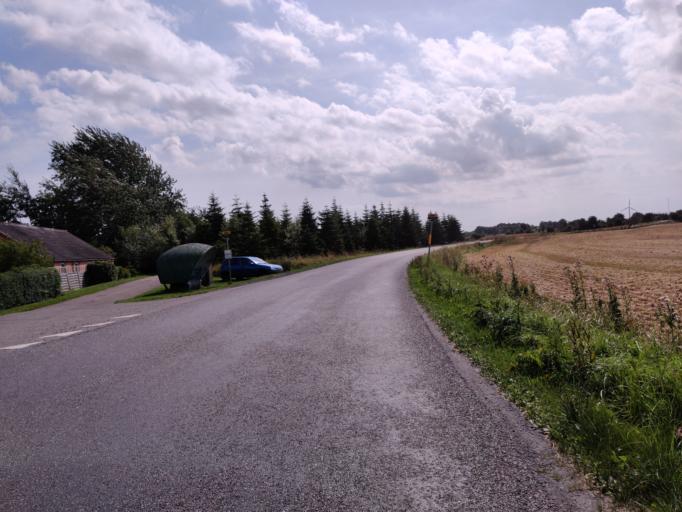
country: DK
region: Zealand
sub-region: Guldborgsund Kommune
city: Nykobing Falster
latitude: 54.6732
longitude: 11.9006
